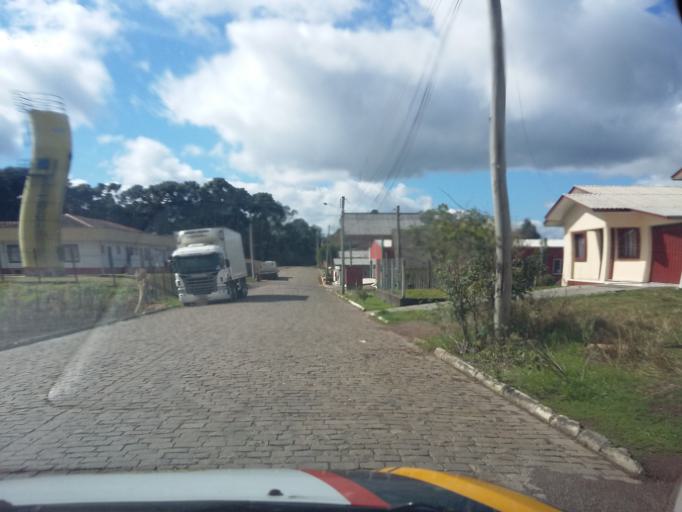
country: BR
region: Rio Grande do Sul
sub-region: Sao Marcos
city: Sao Marcos
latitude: -28.7994
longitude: -51.0931
